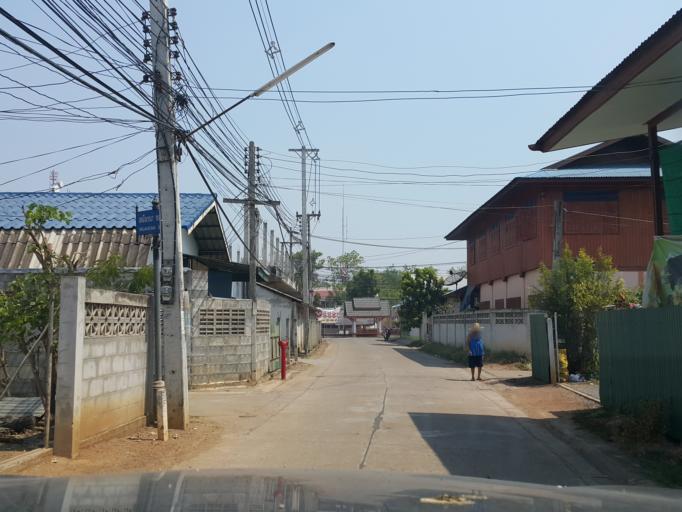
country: TH
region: Sukhothai
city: Thung Saliam
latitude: 17.3198
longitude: 99.5620
